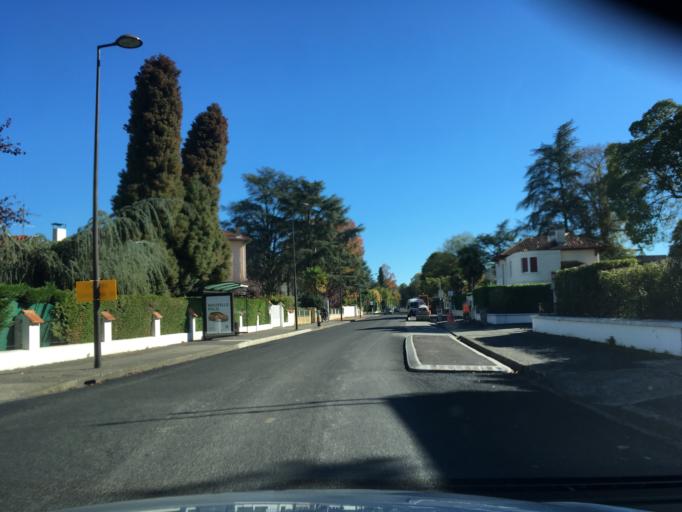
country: FR
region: Aquitaine
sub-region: Departement des Pyrenees-Atlantiques
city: Bizanos
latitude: 43.2990
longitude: -0.3469
